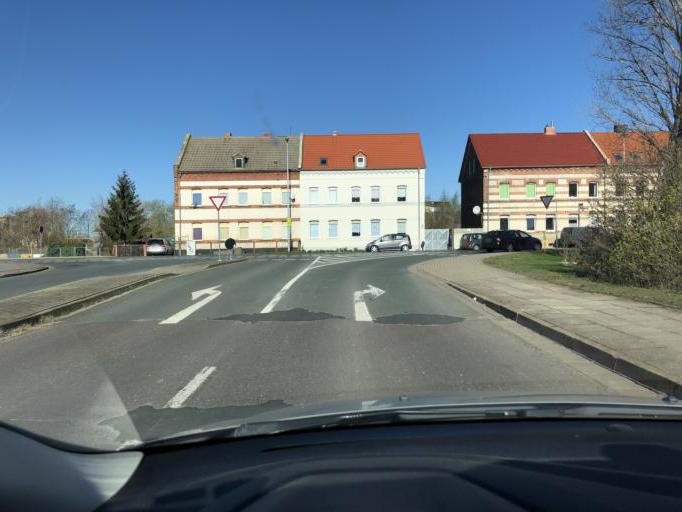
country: DE
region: Saxony-Anhalt
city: Stassfurt
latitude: 51.8603
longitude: 11.5933
